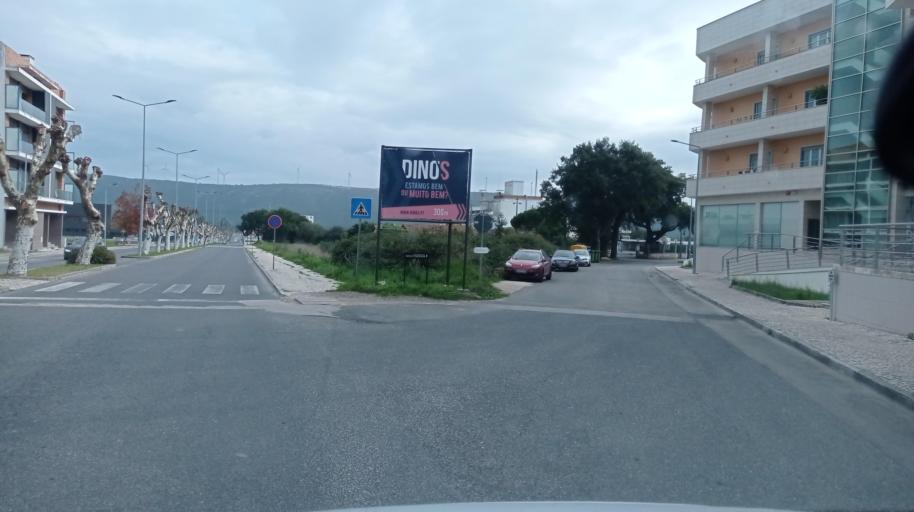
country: PT
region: Leiria
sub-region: Alcobaca
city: Benedita
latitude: 39.4255
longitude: -8.9780
